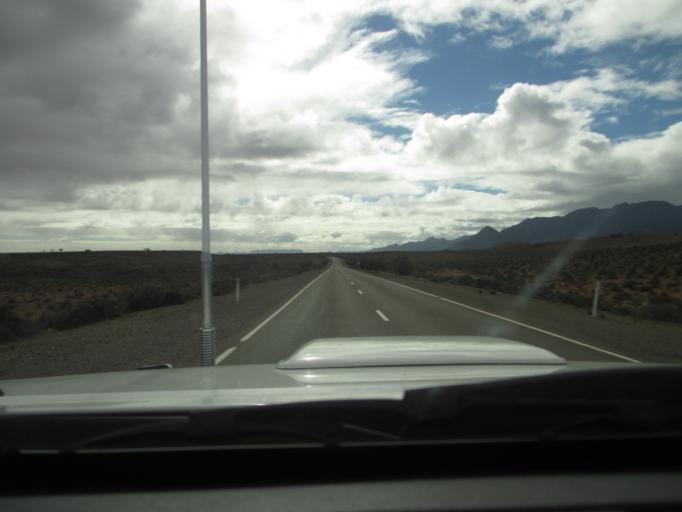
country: AU
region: South Australia
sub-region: Flinders Ranges
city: Quorn
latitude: -31.5703
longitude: 138.4246
